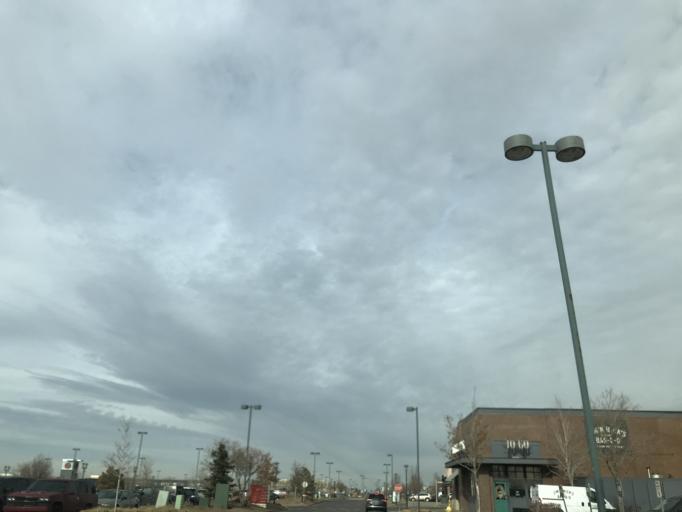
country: US
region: Colorado
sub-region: Adams County
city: Commerce City
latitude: 39.7803
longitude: -104.8932
